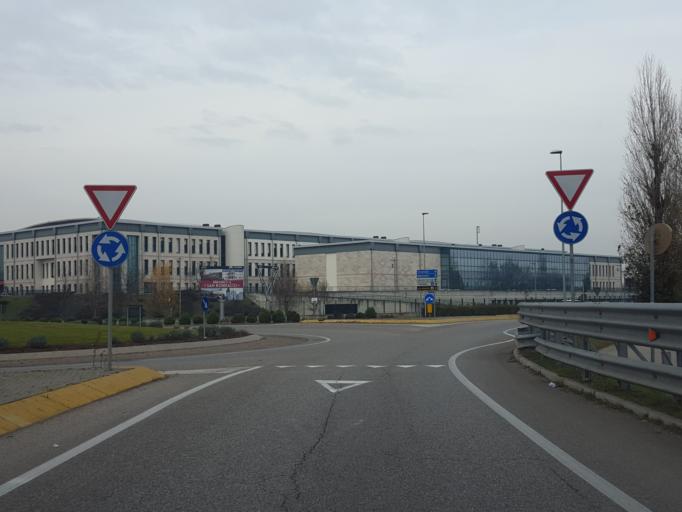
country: IT
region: Veneto
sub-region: Provincia di Verona
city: San Bonifacio
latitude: 45.3898
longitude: 11.2803
